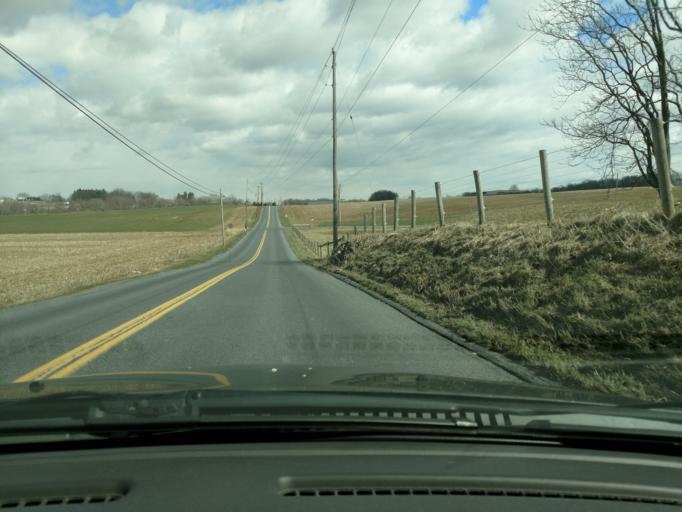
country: US
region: Pennsylvania
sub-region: Lebanon County
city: Myerstown
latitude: 40.3615
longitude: -76.3208
